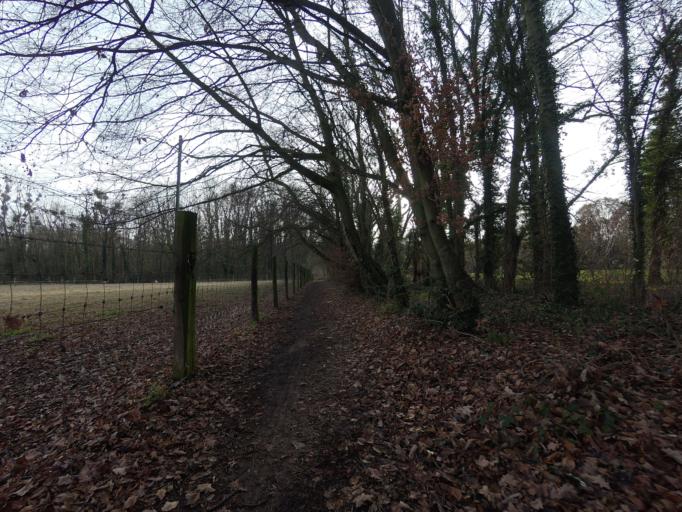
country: BE
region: Flanders
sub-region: Provincie Vlaams-Brabant
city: Kortenberg
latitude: 50.8861
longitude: 4.5511
